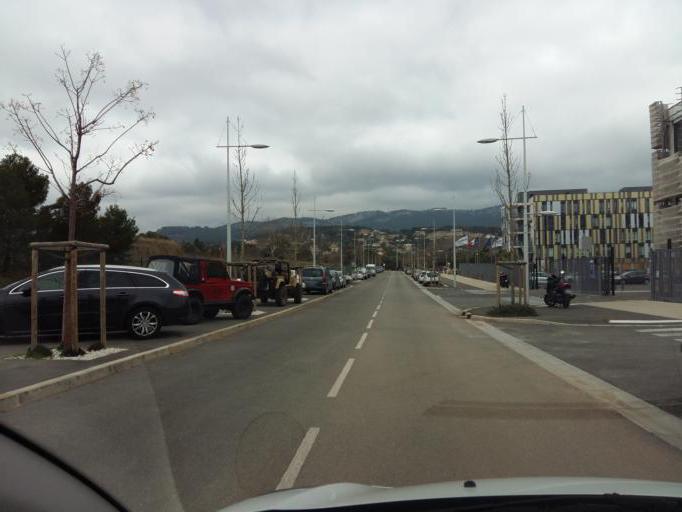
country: FR
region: Provence-Alpes-Cote d'Azur
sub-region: Departement du Var
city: Ollioules
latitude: 43.1244
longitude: 5.8673
